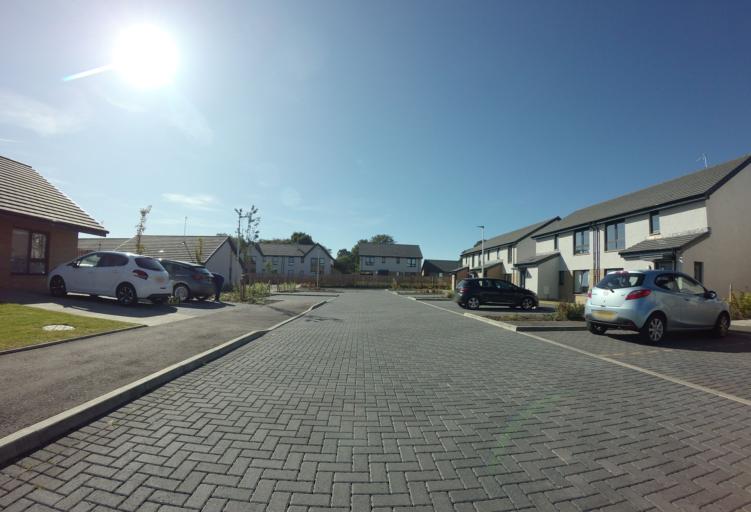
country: GB
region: Scotland
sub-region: West Lothian
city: Livingston
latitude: 55.8981
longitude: -3.5629
